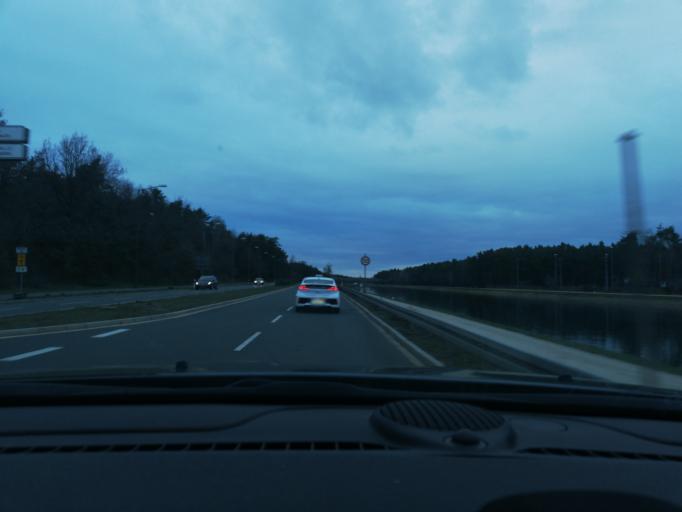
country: DE
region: Bavaria
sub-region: Regierungsbezirk Mittelfranken
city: Erlangen
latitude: 49.6023
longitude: 10.9717
